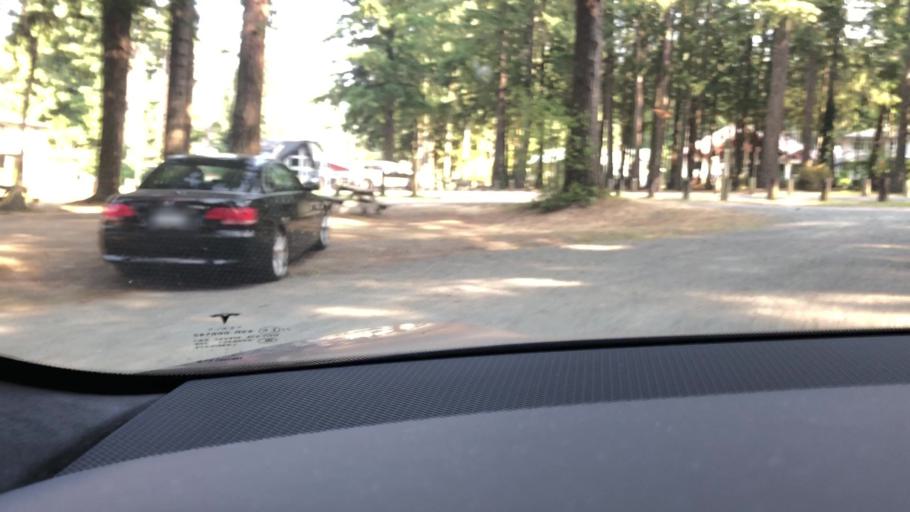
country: CA
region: British Columbia
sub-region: Fraser Valley Regional District
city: Chilliwack
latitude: 49.0672
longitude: -121.9748
